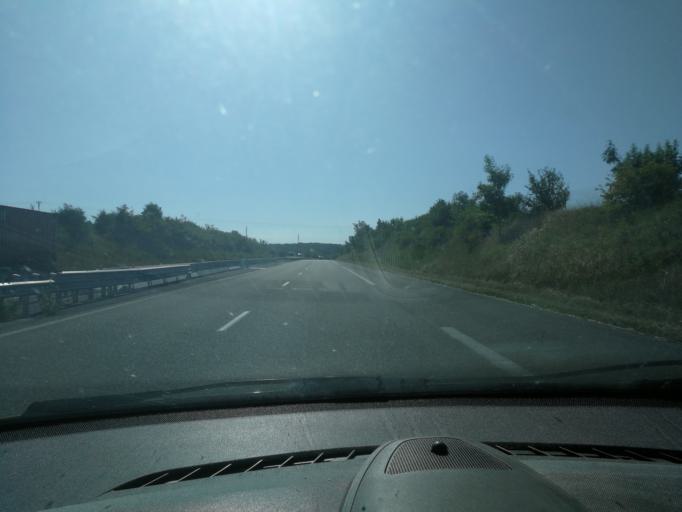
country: FR
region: Alsace
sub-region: Departement du Bas-Rhin
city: Drulingen
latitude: 48.8093
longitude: 7.1666
